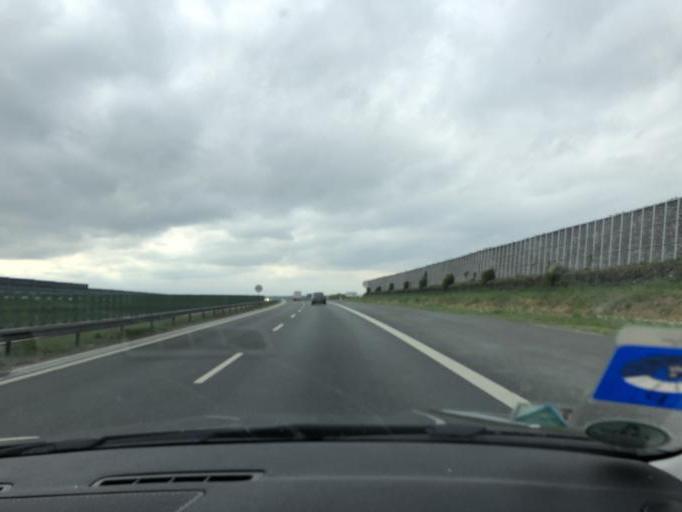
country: PL
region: Opole Voivodeship
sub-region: Powiat krapkowicki
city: Krapkowice
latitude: 50.5126
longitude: 17.9614
